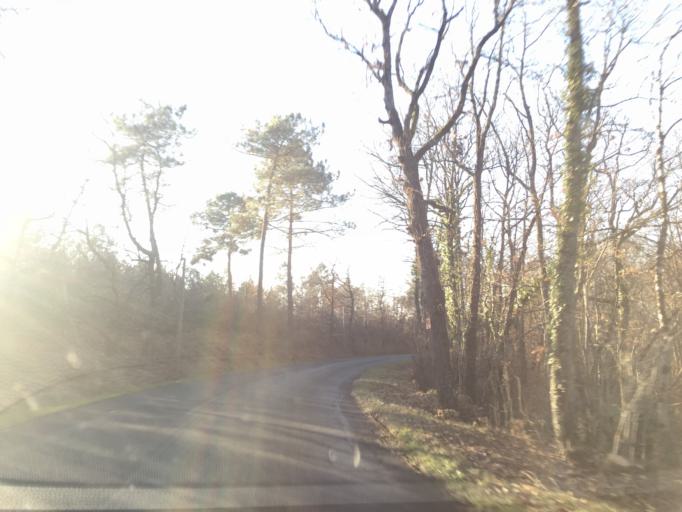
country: FR
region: Aquitaine
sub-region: Departement de la Dordogne
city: Riberac
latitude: 45.2107
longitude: 0.3027
